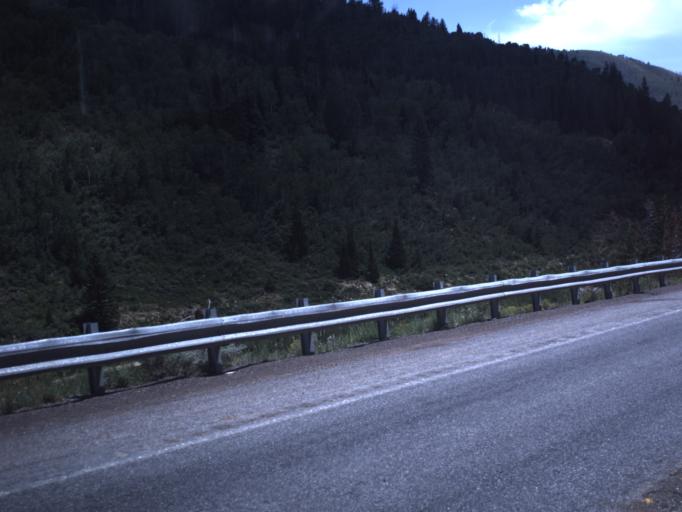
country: US
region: Utah
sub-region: Sanpete County
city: Fairview
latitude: 39.5966
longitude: -111.2067
